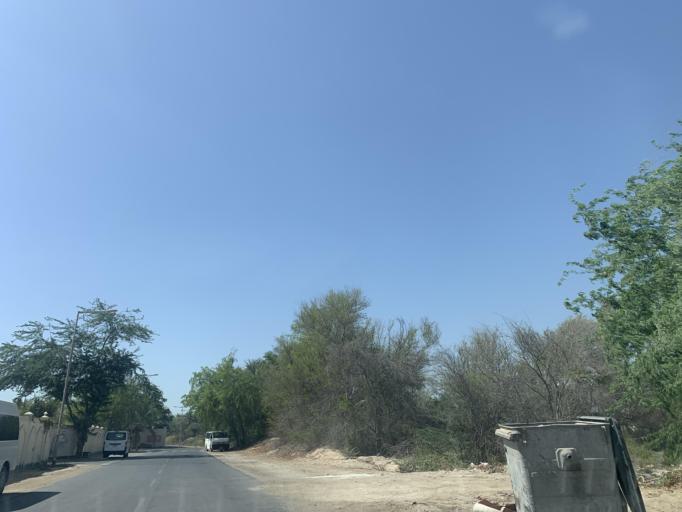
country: BH
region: Manama
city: Jidd Hafs
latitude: 26.2248
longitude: 50.4994
